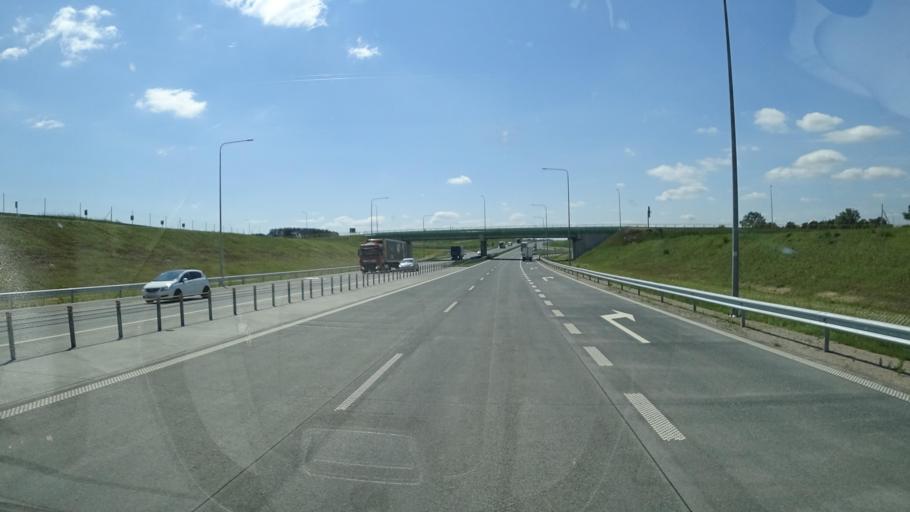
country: PL
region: Podlasie
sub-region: Powiat kolnenski
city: Stawiski
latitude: 53.4592
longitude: 22.1991
